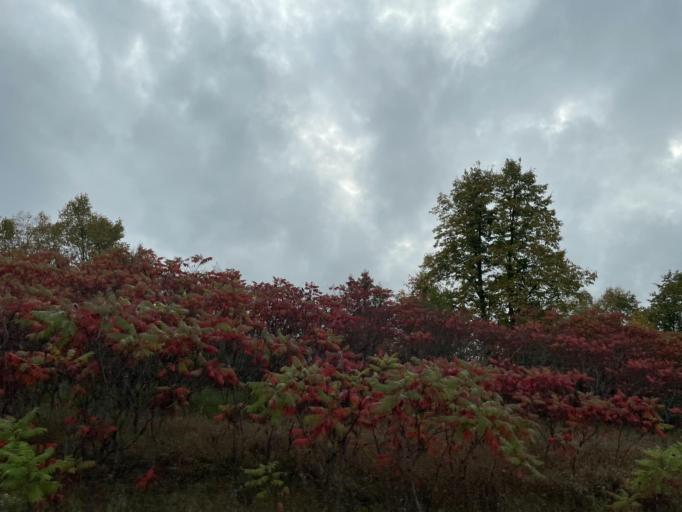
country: CA
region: Ontario
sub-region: Wellington County
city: Guelph
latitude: 43.5564
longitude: -80.1943
